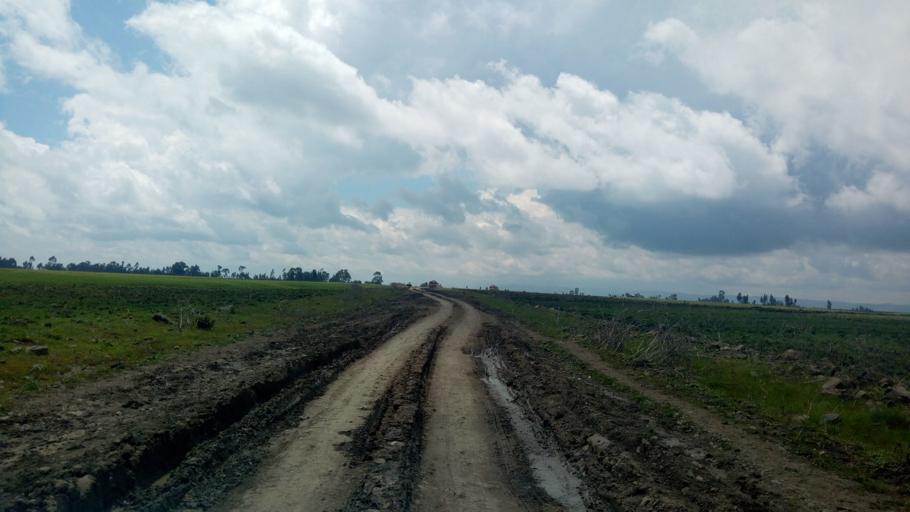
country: ET
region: Oromiya
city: Sendafa
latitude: 9.0068
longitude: 39.1242
